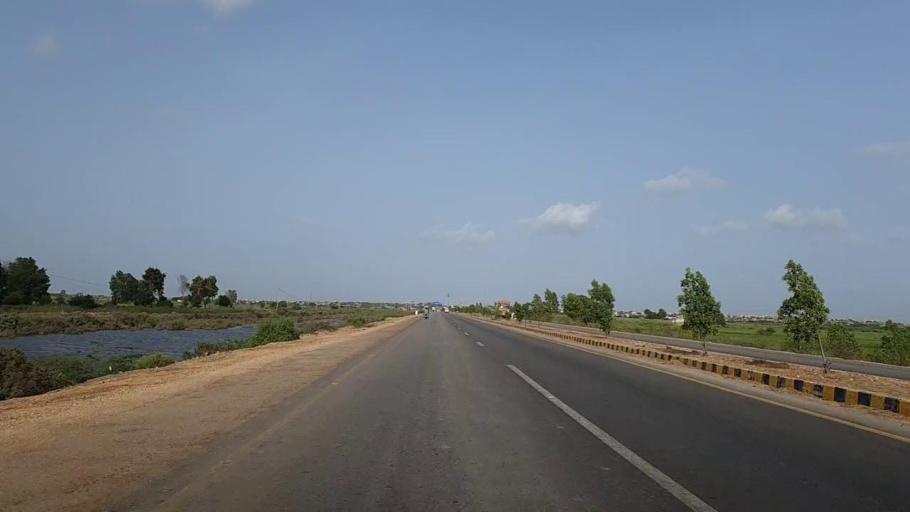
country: PK
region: Sindh
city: Thatta
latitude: 24.7453
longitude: 67.8631
